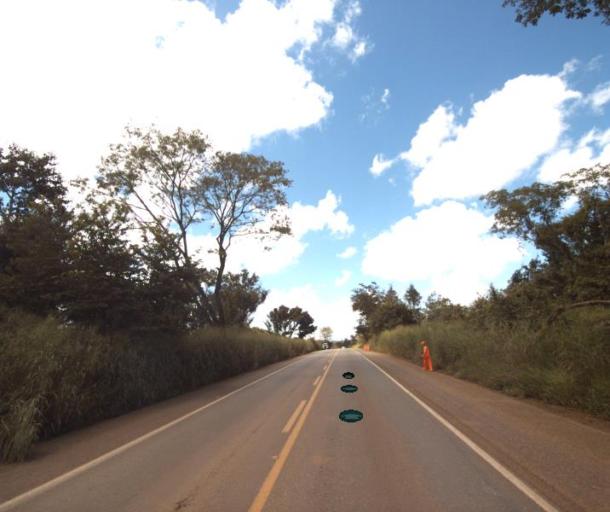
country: BR
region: Goias
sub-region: Petrolina De Goias
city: Petrolina de Goias
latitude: -15.9994
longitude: -49.1418
